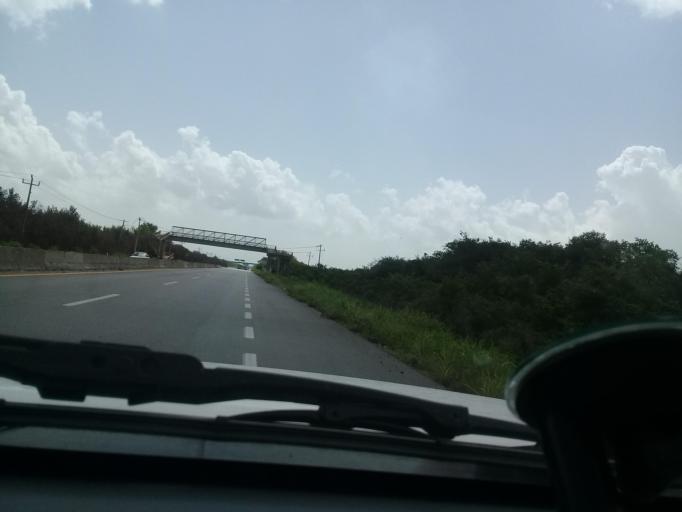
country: MX
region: Veracruz
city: Moralillo
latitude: 22.2123
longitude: -97.9579
